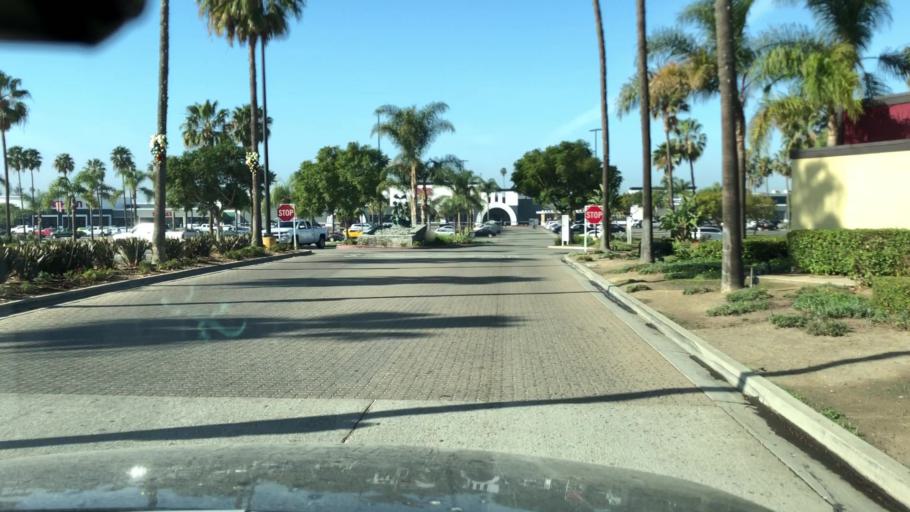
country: US
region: California
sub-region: Ventura County
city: El Rio
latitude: 34.2222
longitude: -119.1592
